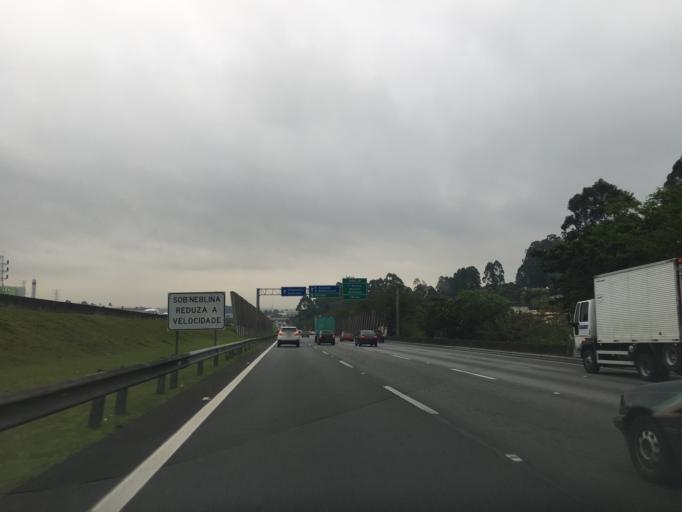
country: BR
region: Sao Paulo
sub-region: Carapicuiba
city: Carapicuiba
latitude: -23.4927
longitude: -46.8113
